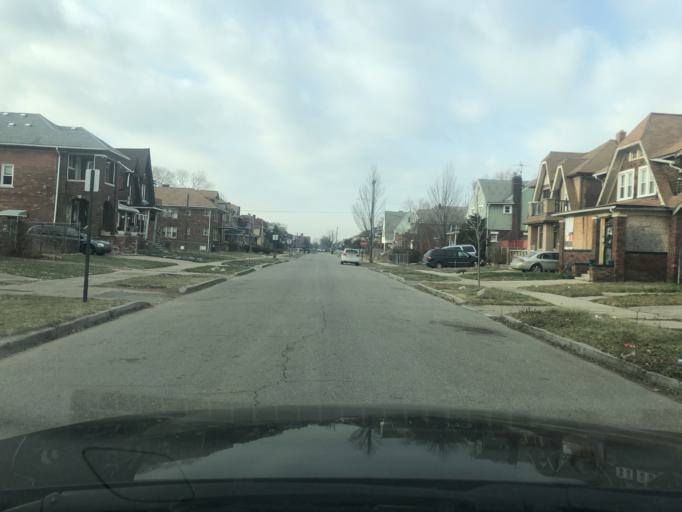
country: US
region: Michigan
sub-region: Wayne County
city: Highland Park
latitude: 42.3946
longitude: -83.1255
